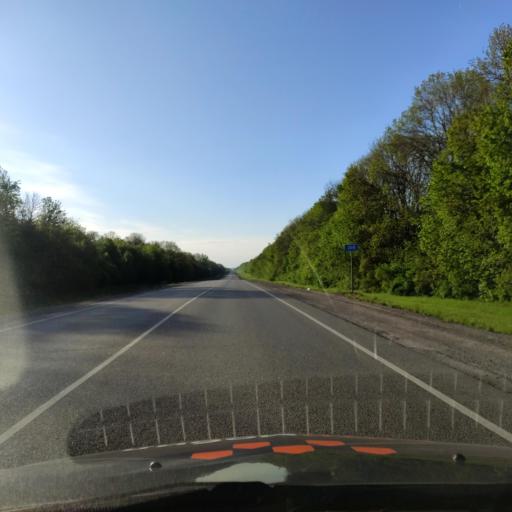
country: RU
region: Lipetsk
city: Yelets
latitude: 52.5748
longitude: 38.6502
